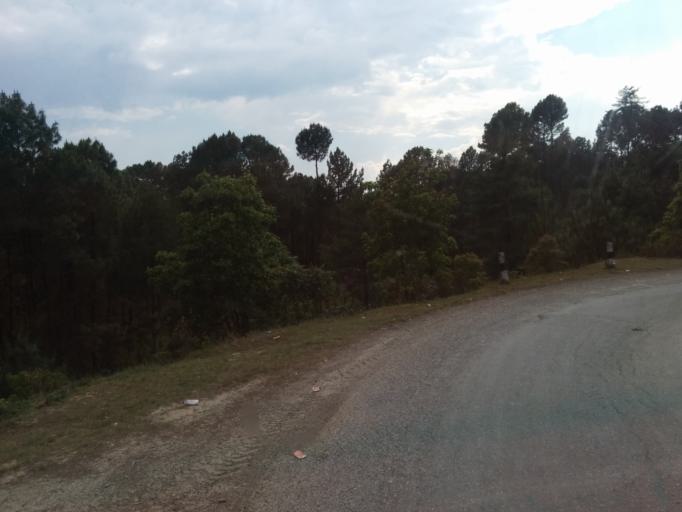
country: NP
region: Central Region
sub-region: Bagmati Zone
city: Nagarkot
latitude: 27.7099
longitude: 85.4886
